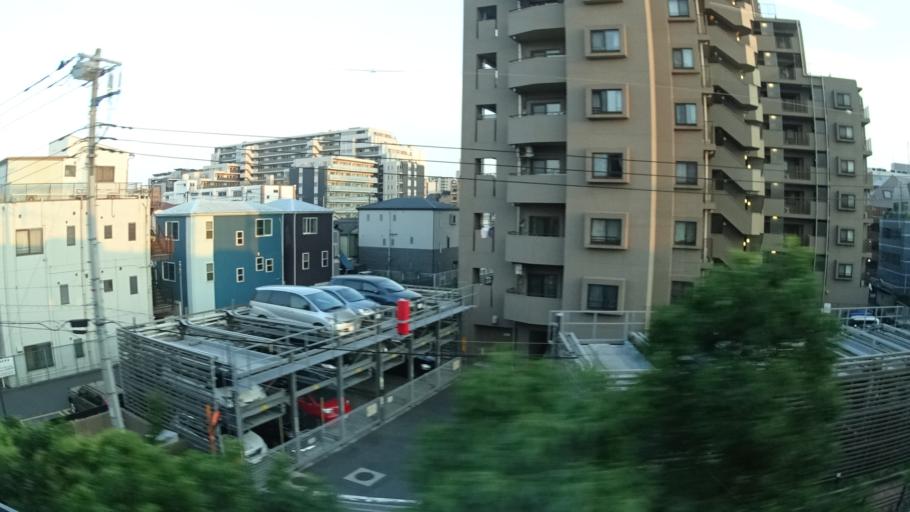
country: JP
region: Saitama
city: Soka
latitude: 35.7337
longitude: 139.7728
